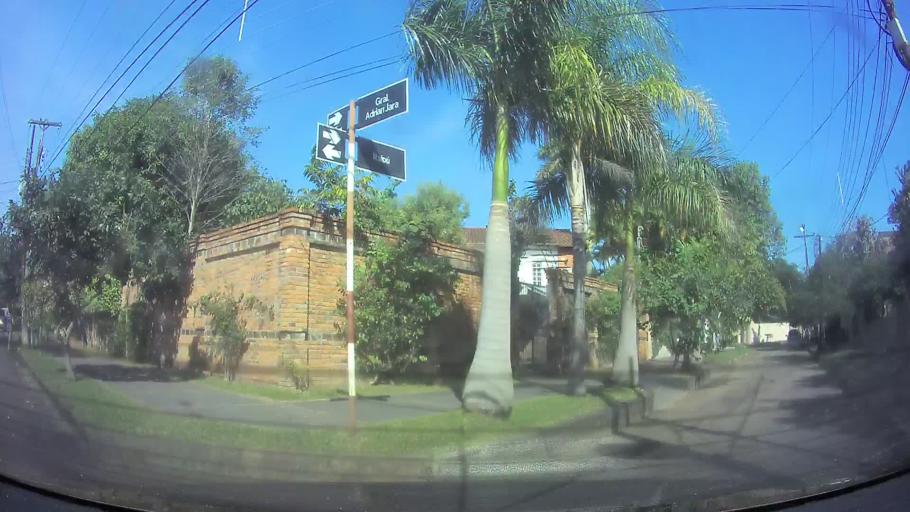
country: PY
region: Central
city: Fernando de la Mora
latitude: -25.2822
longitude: -57.5424
